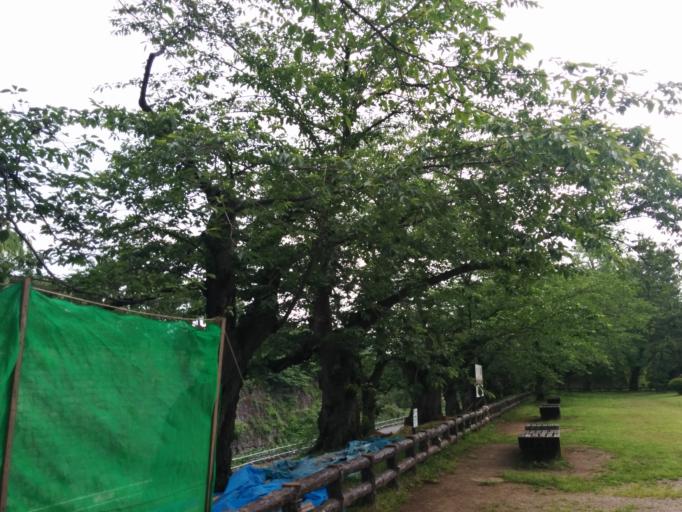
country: JP
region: Aomori
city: Hirosaki
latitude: 40.6076
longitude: 140.4646
